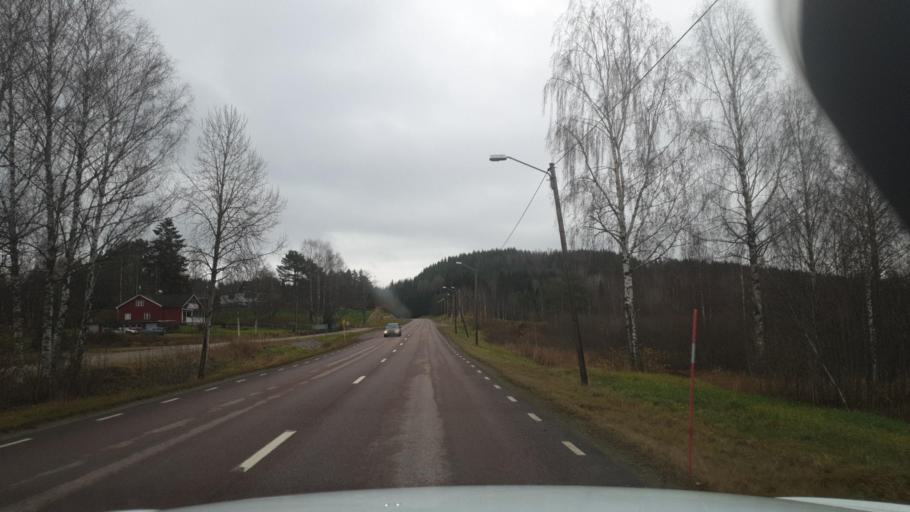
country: SE
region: Vaermland
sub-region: Eda Kommun
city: Amotfors
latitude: 59.6754
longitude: 12.4267
